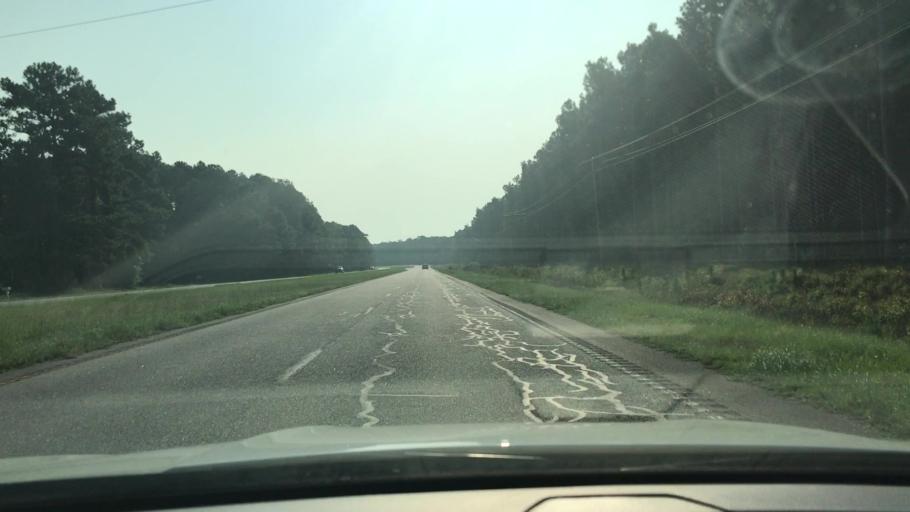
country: US
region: South Carolina
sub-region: Charleston County
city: Awendaw
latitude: 33.0460
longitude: -79.5727
